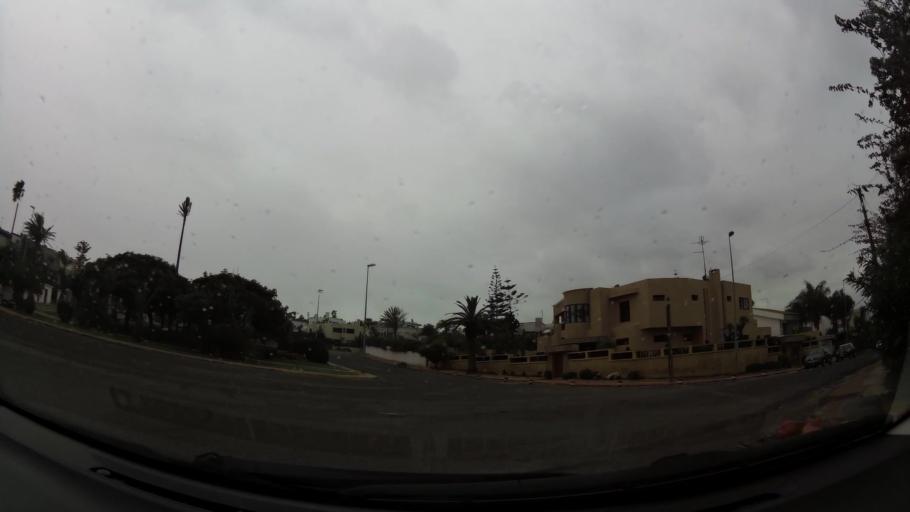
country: MA
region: Grand Casablanca
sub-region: Casablanca
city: Casablanca
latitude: 33.5947
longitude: -7.6629
